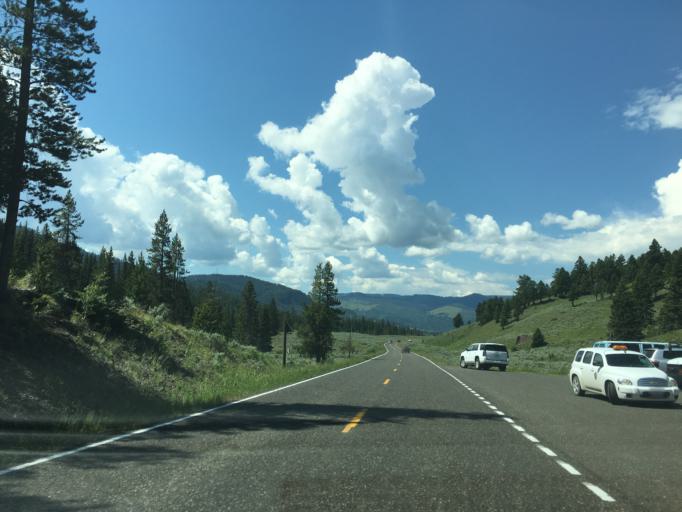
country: US
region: Montana
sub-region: Park County
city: Livingston
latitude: 44.8994
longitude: -110.1227
